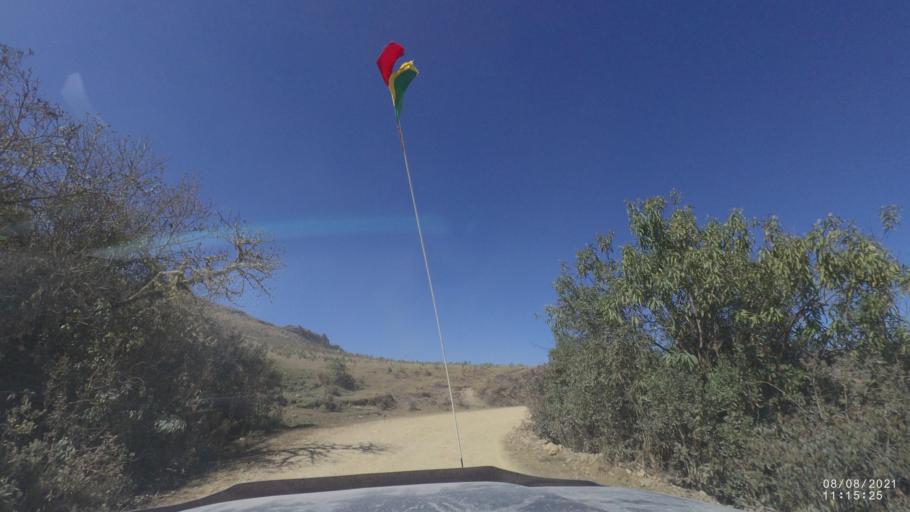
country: BO
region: Cochabamba
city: Colchani
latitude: -16.7750
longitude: -66.6669
